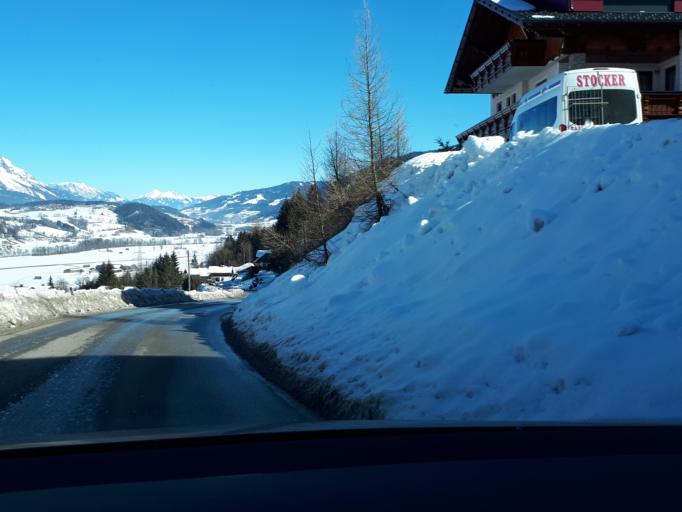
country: AT
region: Styria
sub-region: Politischer Bezirk Liezen
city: Pruggern
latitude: 47.4174
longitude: 13.8717
